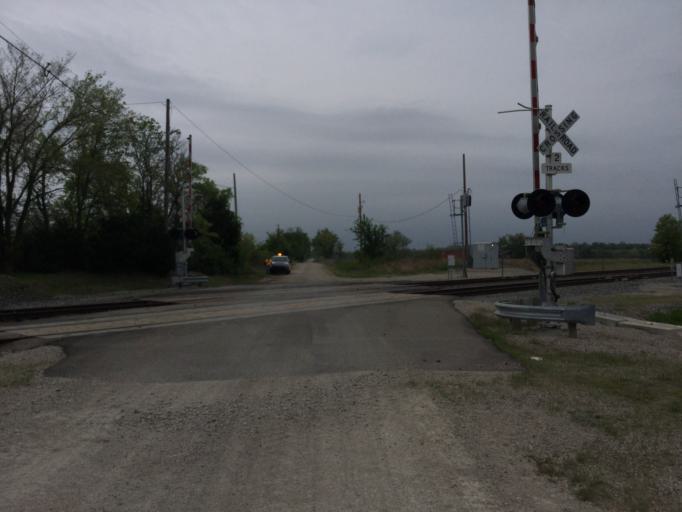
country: US
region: Kansas
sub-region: Labette County
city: Parsons
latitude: 37.3760
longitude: -95.2670
